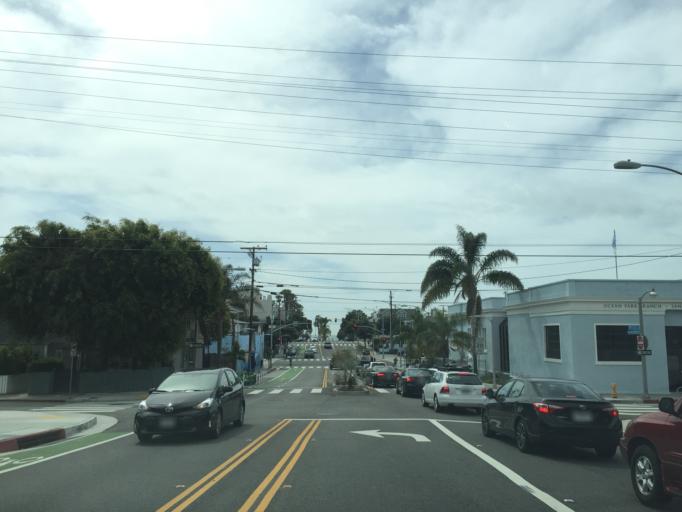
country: US
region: California
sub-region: Los Angeles County
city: Santa Monica
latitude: 34.0030
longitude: -118.4830
